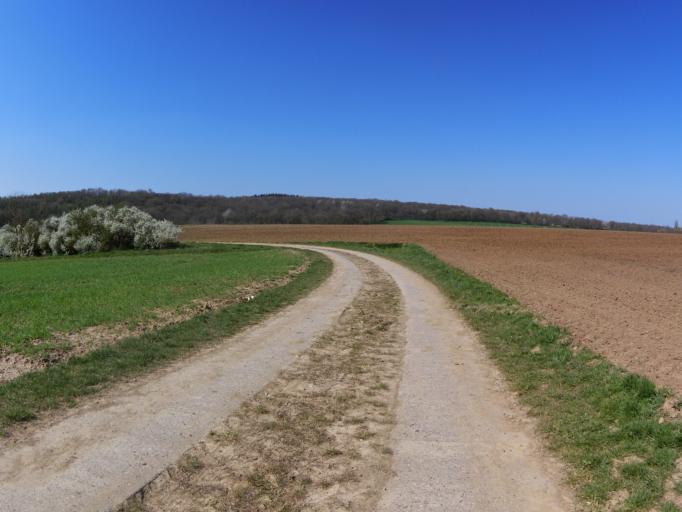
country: DE
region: Bavaria
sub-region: Regierungsbezirk Unterfranken
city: Rottendorf
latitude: 49.8177
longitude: 10.0713
